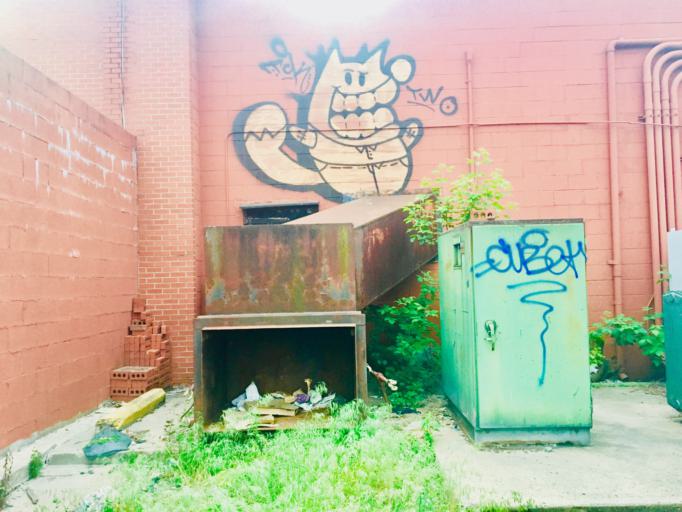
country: US
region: Michigan
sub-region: Wayne County
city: River Rouge
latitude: 42.3137
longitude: -83.1259
